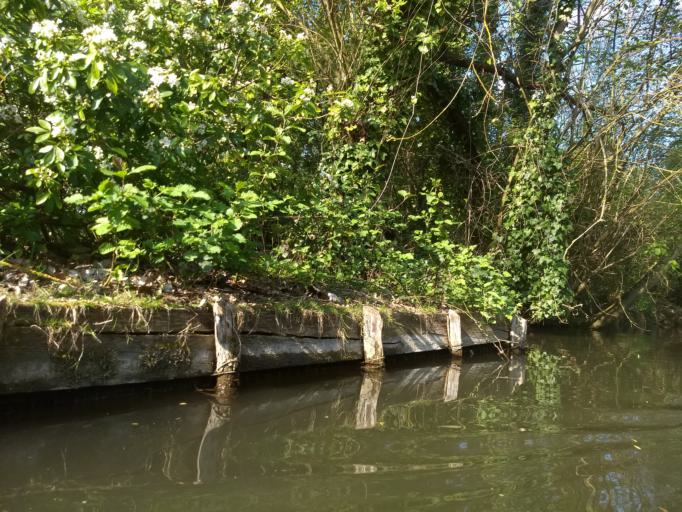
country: FR
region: Picardie
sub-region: Departement de la Somme
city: Rivery
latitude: 49.8961
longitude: 2.3212
